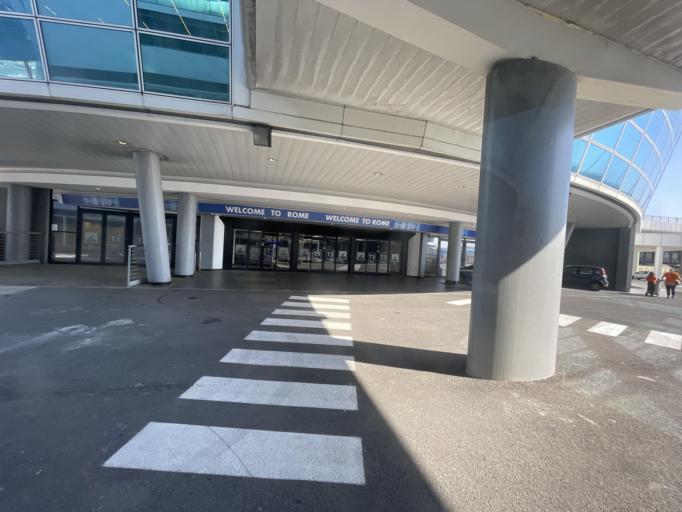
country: IT
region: Latium
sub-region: Citta metropolitana di Roma Capitale
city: Fiumicino-Isola Sacra
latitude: 41.7955
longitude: 12.2483
